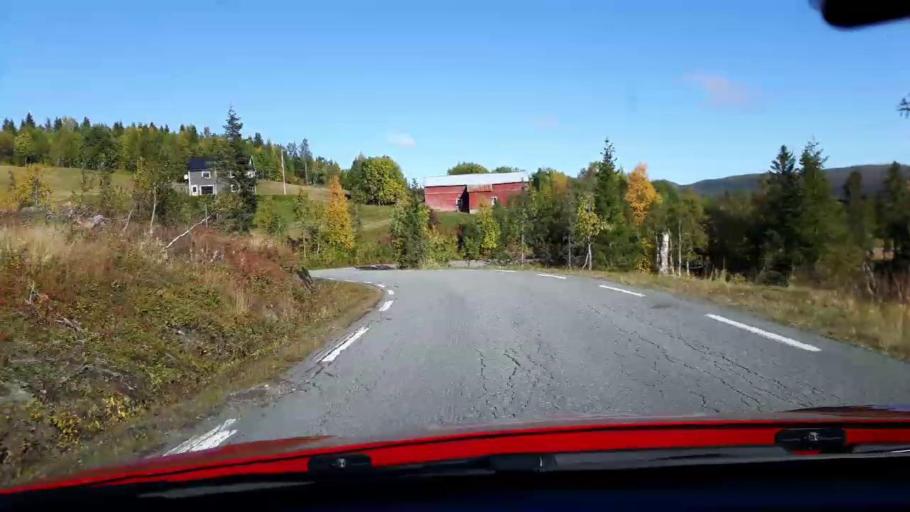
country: NO
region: Nord-Trondelag
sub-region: Lierne
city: Sandvika
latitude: 64.6304
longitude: 13.6908
